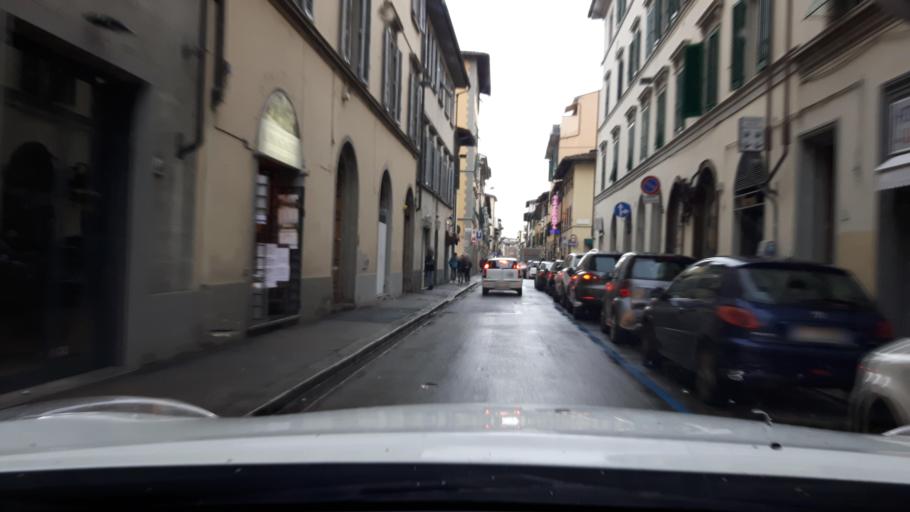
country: IT
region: Tuscany
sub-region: Province of Florence
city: Florence
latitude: 43.7700
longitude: 11.2775
